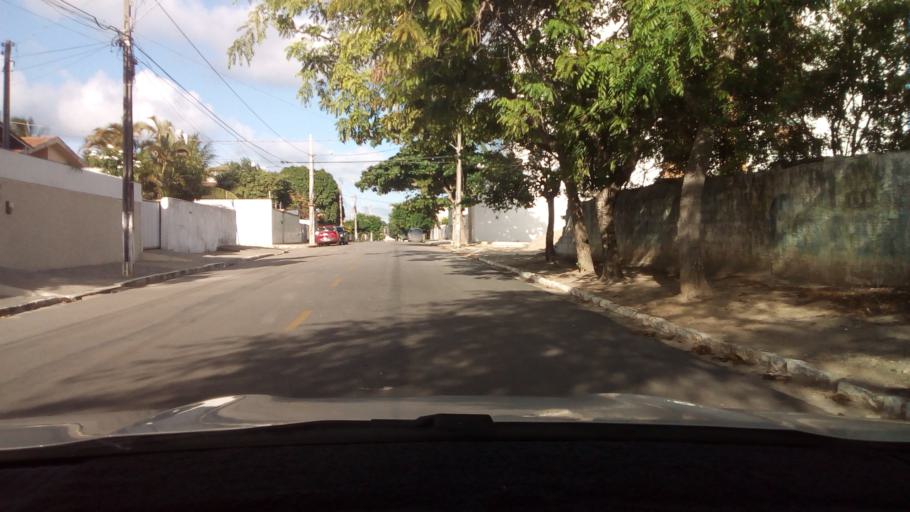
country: BR
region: Paraiba
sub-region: Joao Pessoa
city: Joao Pessoa
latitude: -7.1373
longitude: -34.8332
